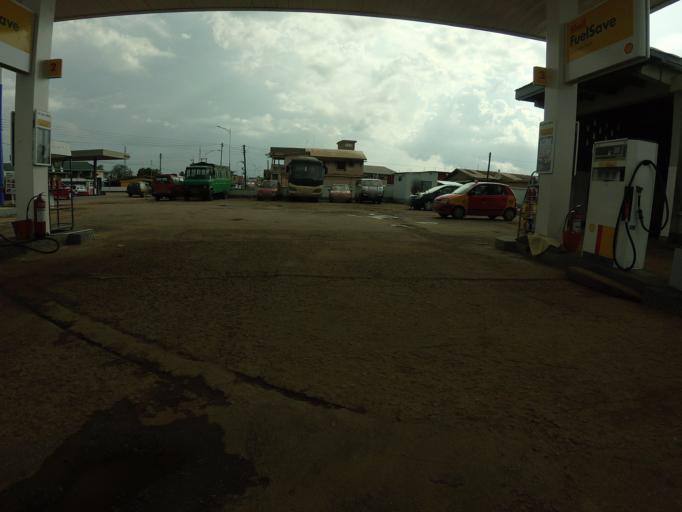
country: GH
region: Volta
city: Hohoe
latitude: 7.1508
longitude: 0.4713
